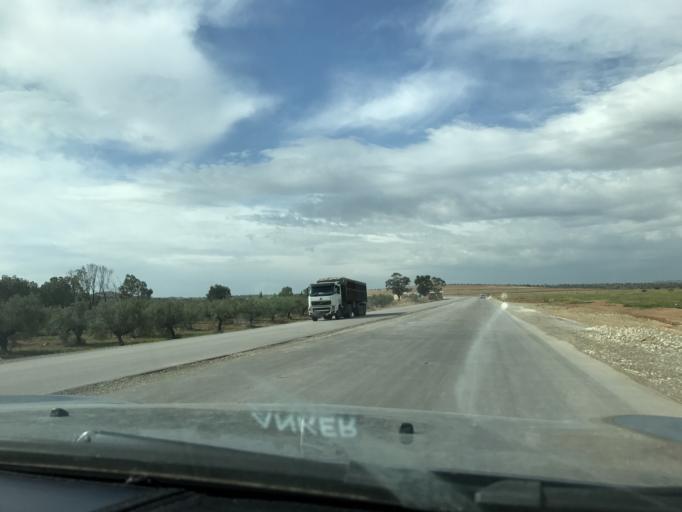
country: TN
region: Zaghwan
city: El Fahs
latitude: 36.3148
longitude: 9.8199
